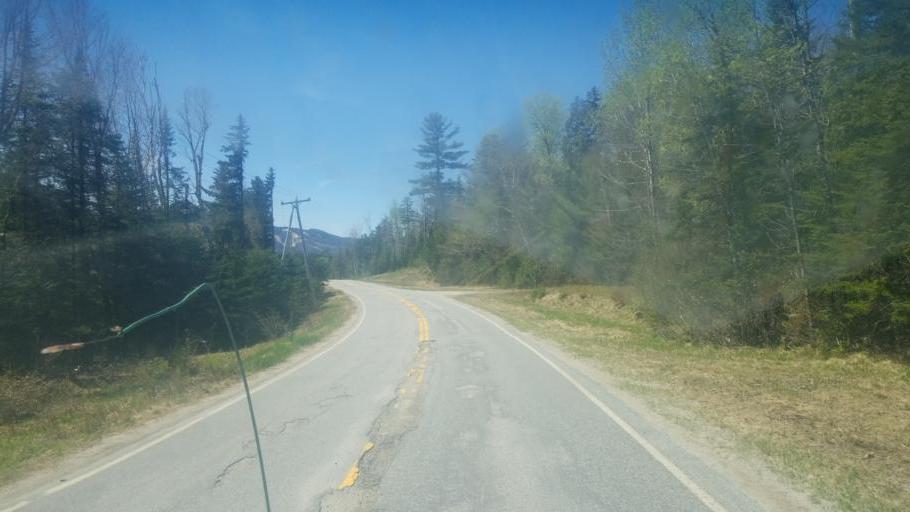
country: US
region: New Hampshire
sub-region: Coos County
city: Jefferson
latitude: 44.2679
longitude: -71.4125
